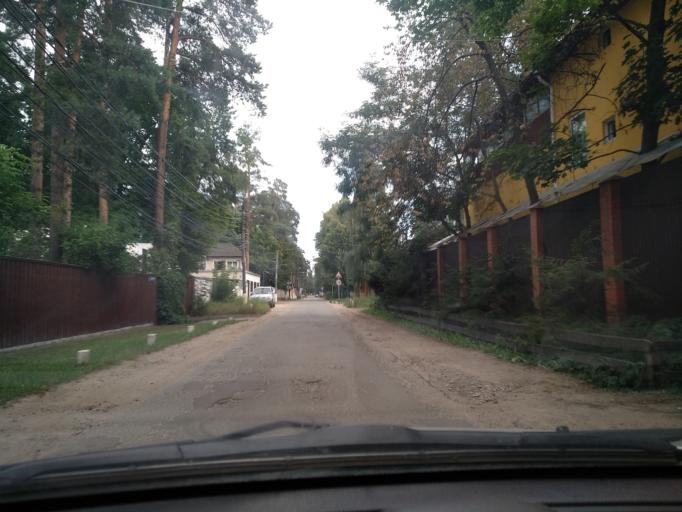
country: RU
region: Moskovskaya
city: Bykovo
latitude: 55.6140
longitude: 38.0957
